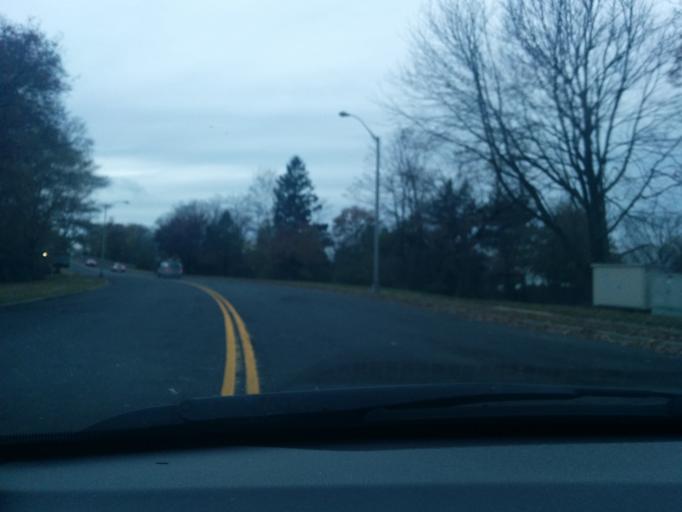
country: US
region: New Jersey
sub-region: Monmouth County
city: Monmouth Beach
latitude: 40.3199
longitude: -73.9924
